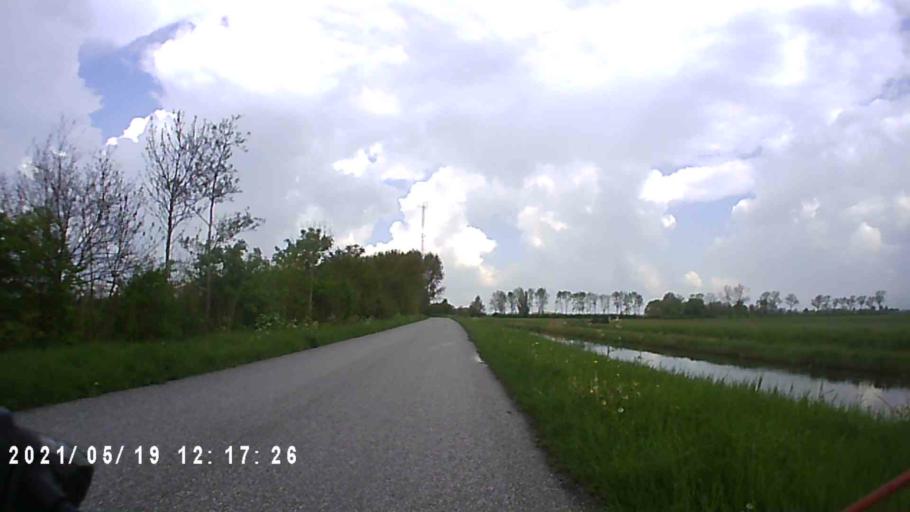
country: NL
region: Friesland
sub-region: Gemeente Kollumerland en Nieuwkruisland
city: Kollum
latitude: 53.2581
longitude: 6.1757
